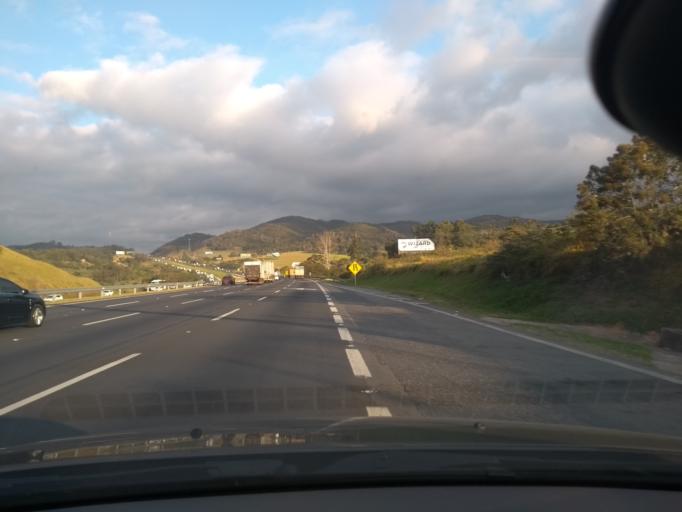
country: BR
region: Sao Paulo
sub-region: Jundiai
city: Jundiai
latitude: -23.2083
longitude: -46.9250
